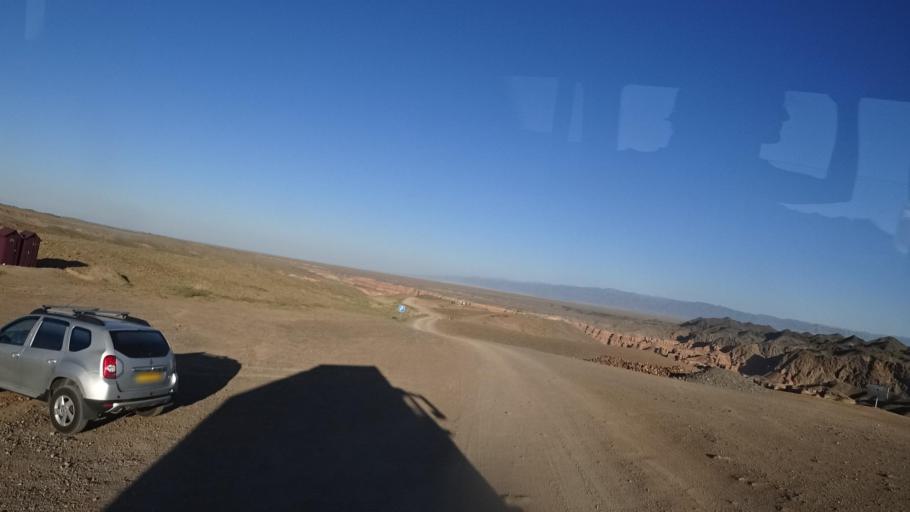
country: KZ
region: Almaty Oblysy
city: Kegen
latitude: 43.3553
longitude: 79.0618
